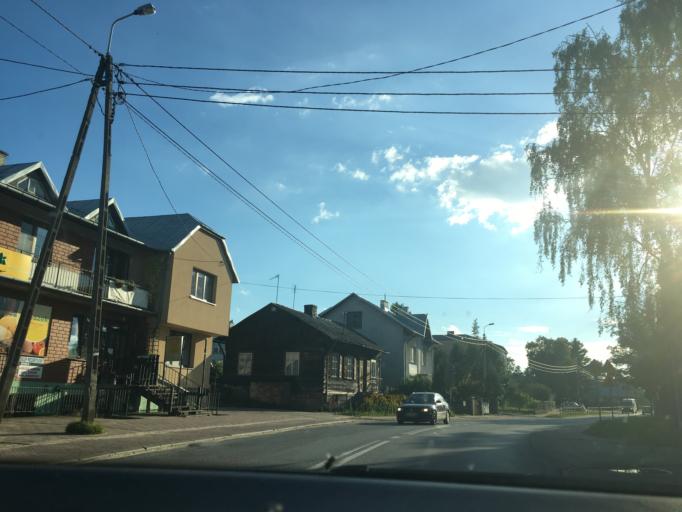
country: PL
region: Masovian Voivodeship
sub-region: Powiat losicki
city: Sarnaki
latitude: 52.3147
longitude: 22.8891
